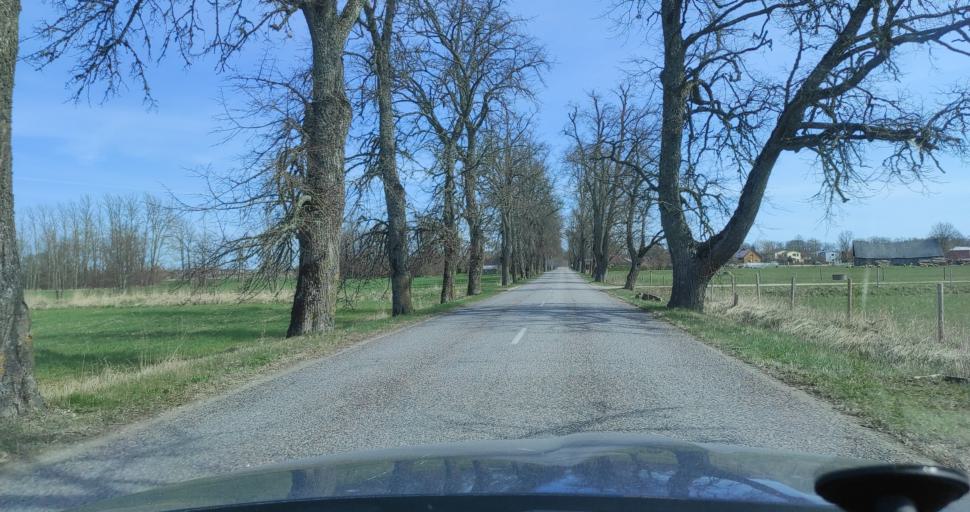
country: LV
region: Talsu Rajons
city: Stende
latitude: 57.2203
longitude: 22.5077
